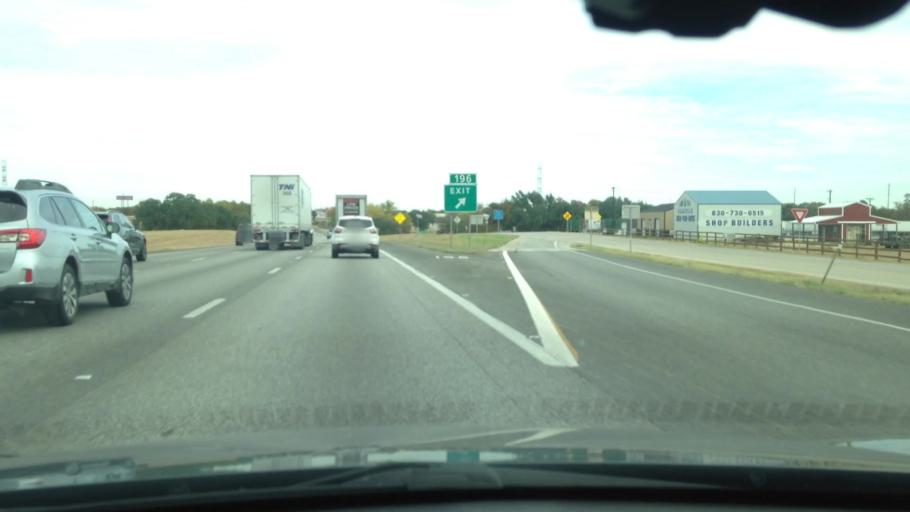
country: US
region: Texas
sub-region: Guadalupe County
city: Redwood
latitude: 29.7899
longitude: -98.0258
